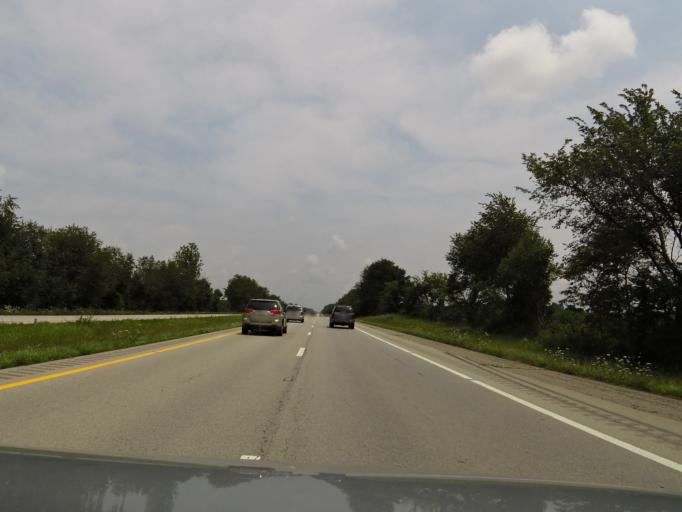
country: US
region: Kentucky
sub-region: Hardin County
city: Elizabethtown
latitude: 37.6226
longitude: -85.9492
